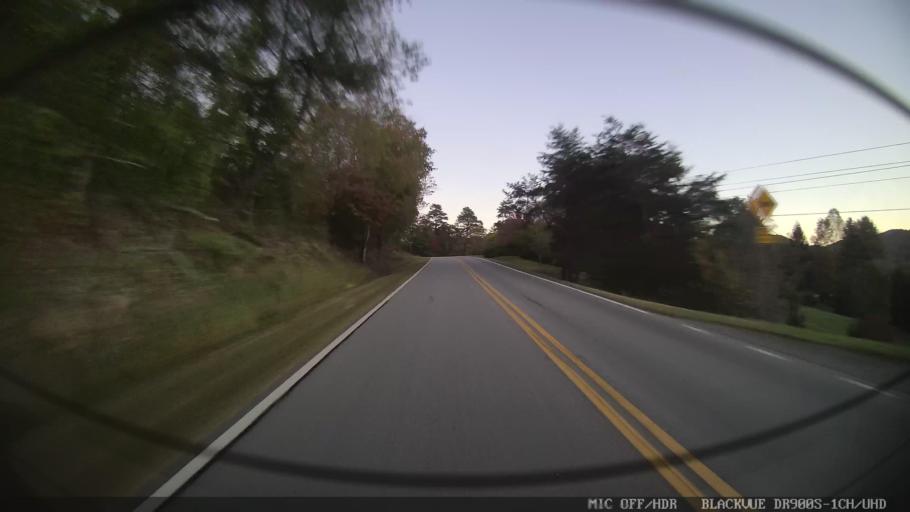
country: US
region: North Carolina
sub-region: Clay County
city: Hayesville
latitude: 34.9575
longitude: -83.8689
